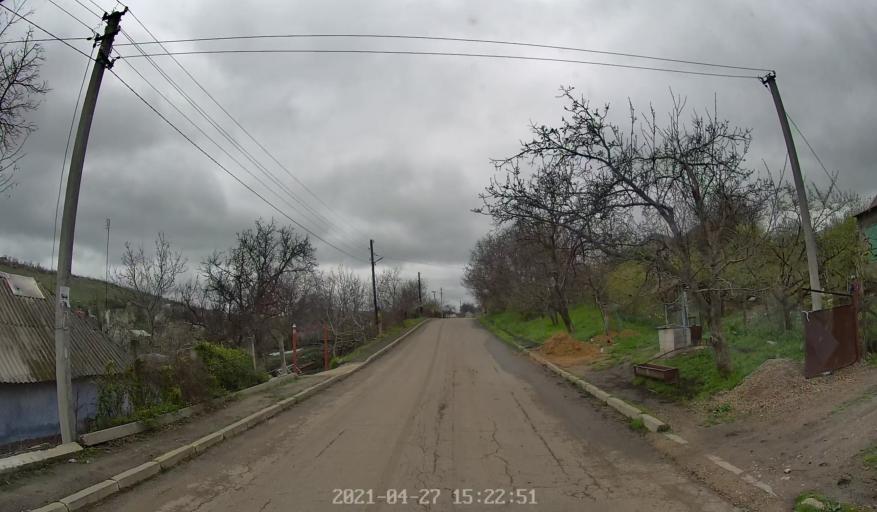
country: MD
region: Chisinau
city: Vadul lui Voda
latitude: 47.0262
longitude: 29.0248
